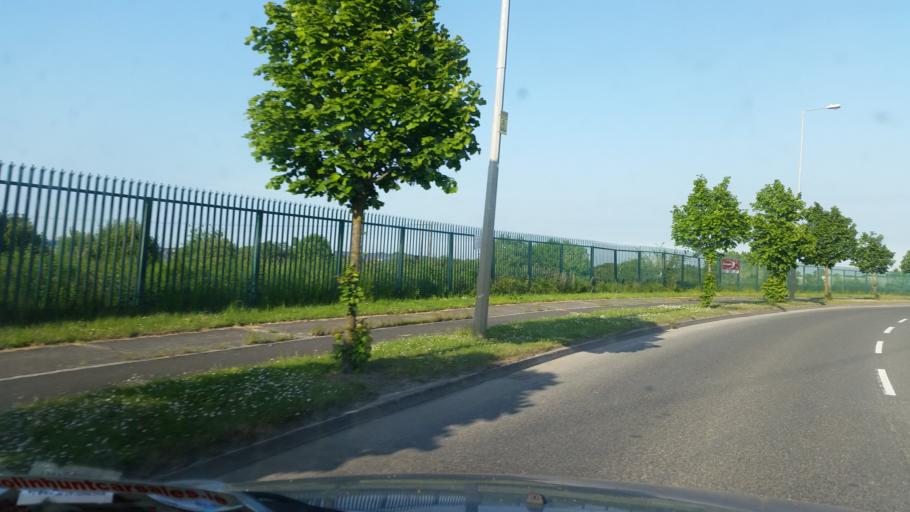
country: IE
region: Leinster
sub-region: Fingal County
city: Blanchardstown
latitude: 53.4156
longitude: -6.3560
